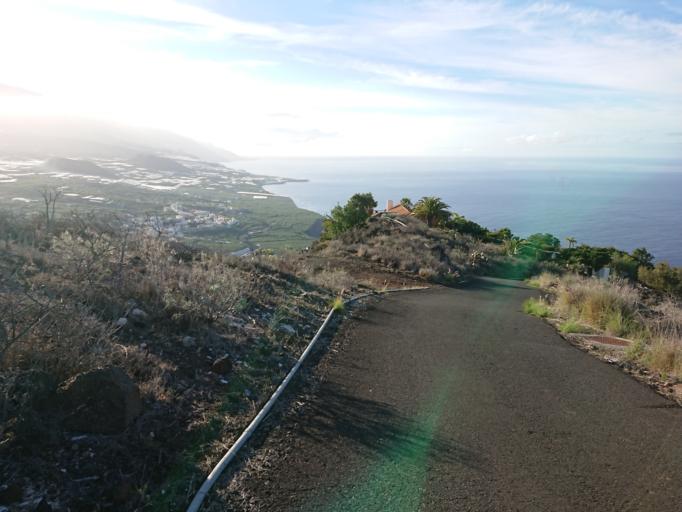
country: ES
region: Canary Islands
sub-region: Provincia de Santa Cruz de Tenerife
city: Tazacorte
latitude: 28.6599
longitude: -17.9436
